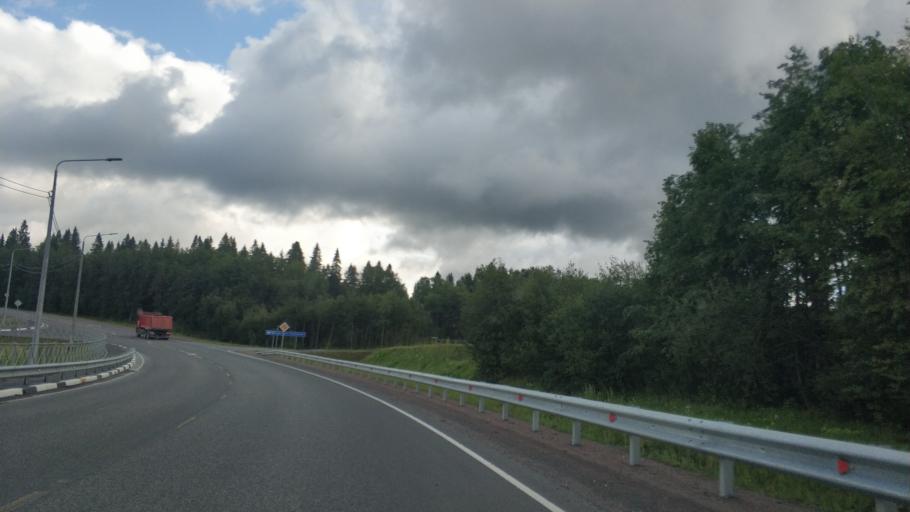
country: RU
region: Republic of Karelia
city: Ruskeala
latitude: 61.9453
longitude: 30.5980
